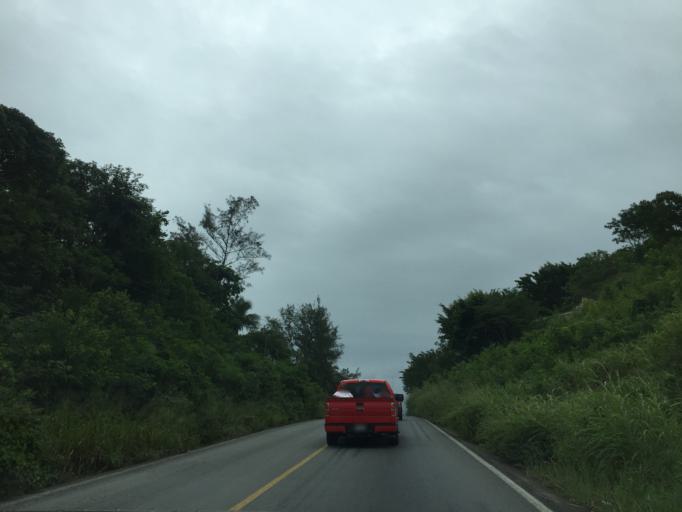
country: MX
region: Veracruz
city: Coatzintla
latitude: 20.4513
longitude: -97.4103
